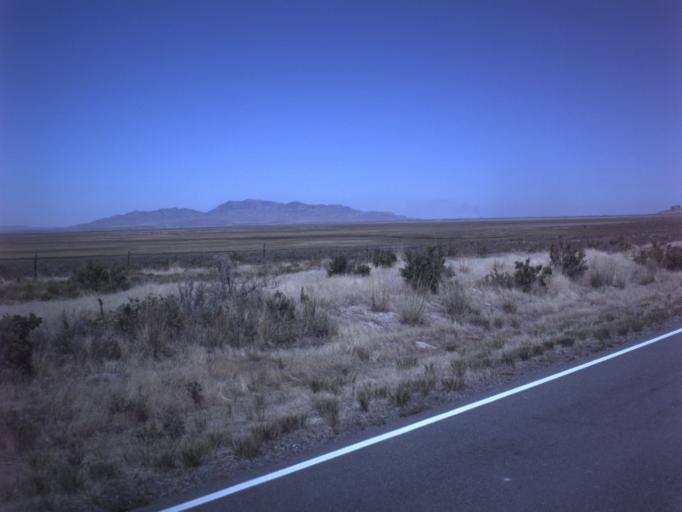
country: US
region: Utah
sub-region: Tooele County
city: Grantsville
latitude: 40.6334
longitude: -112.6937
